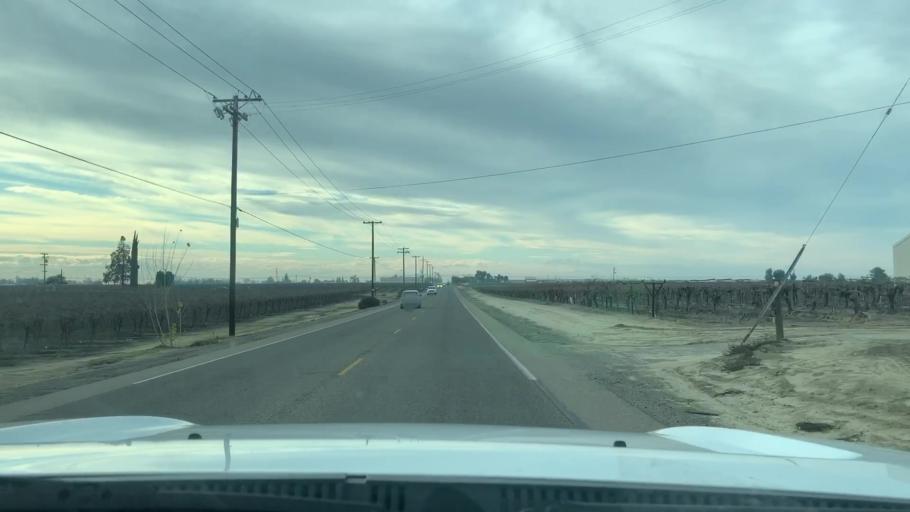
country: US
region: California
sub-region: Fresno County
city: Fowler
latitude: 36.6055
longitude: -119.7318
